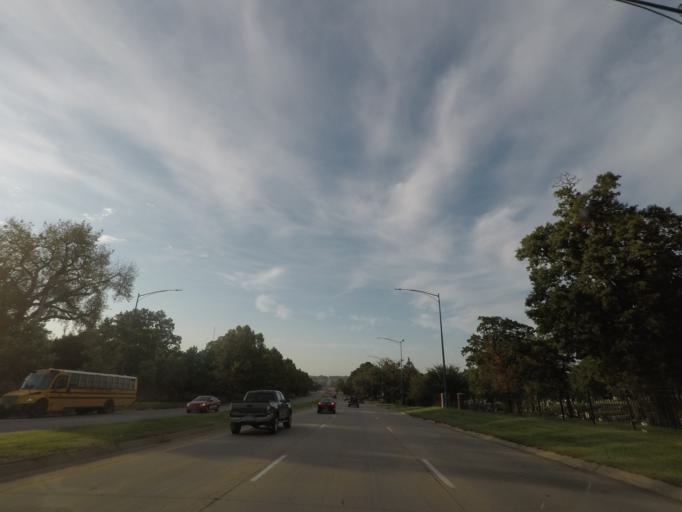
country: US
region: Iowa
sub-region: Polk County
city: Des Moines
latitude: 41.5919
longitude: -93.6448
